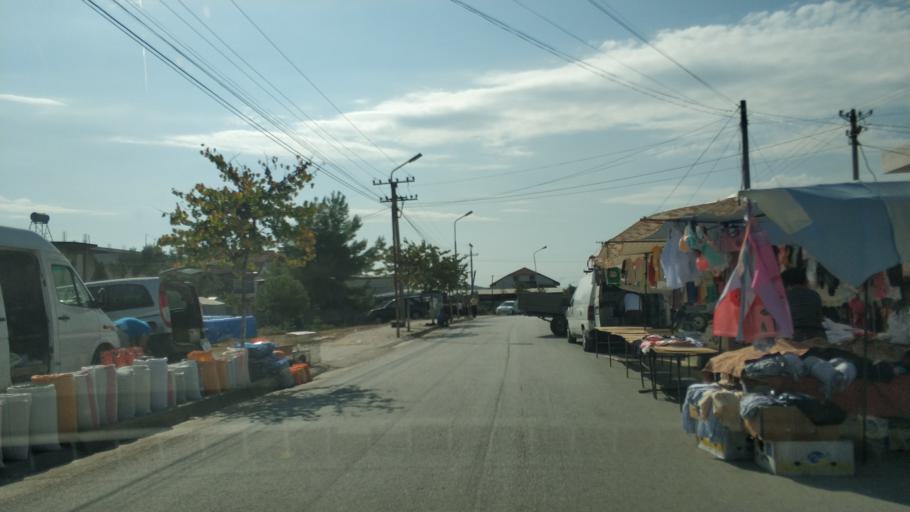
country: AL
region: Fier
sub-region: Rrethi i Lushnjes
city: Divjake
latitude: 40.9926
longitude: 19.5336
